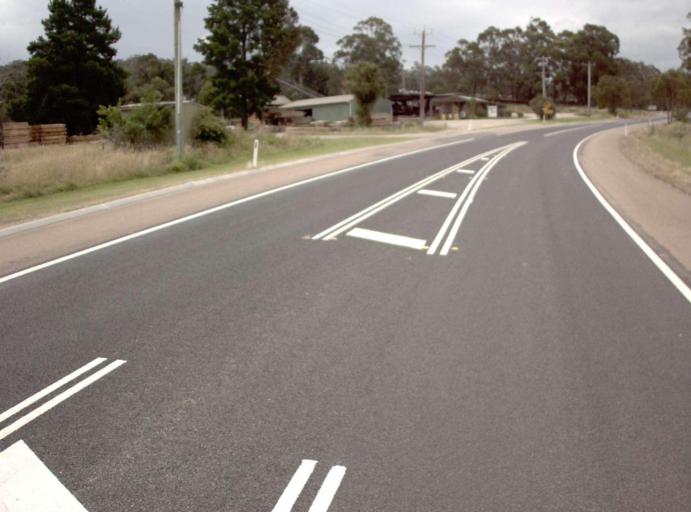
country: AU
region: Victoria
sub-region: East Gippsland
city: Lakes Entrance
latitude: -37.7291
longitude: 148.0890
